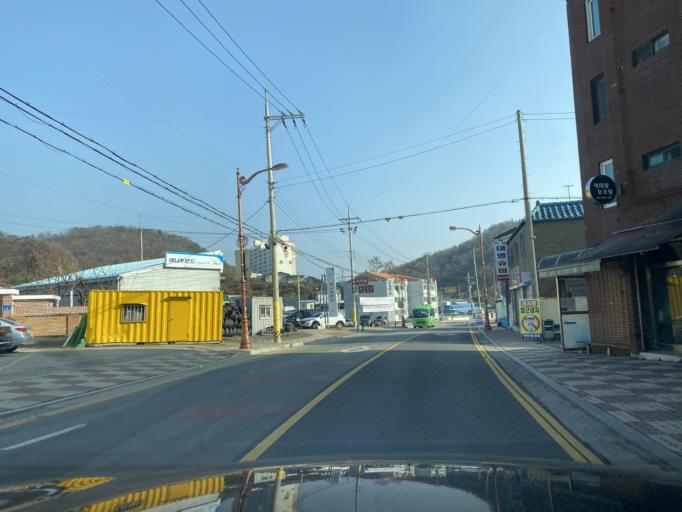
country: KR
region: Chungcheongnam-do
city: Yesan
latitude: 36.6821
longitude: 126.8505
